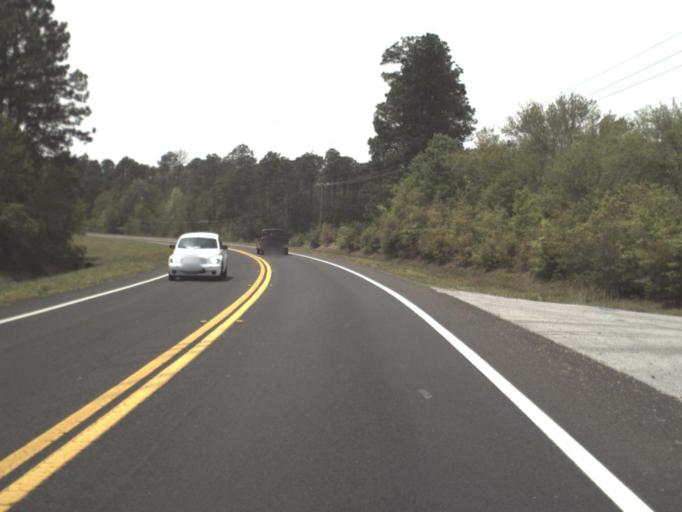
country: US
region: Florida
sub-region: Escambia County
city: Bellview
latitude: 30.4870
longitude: -87.3193
